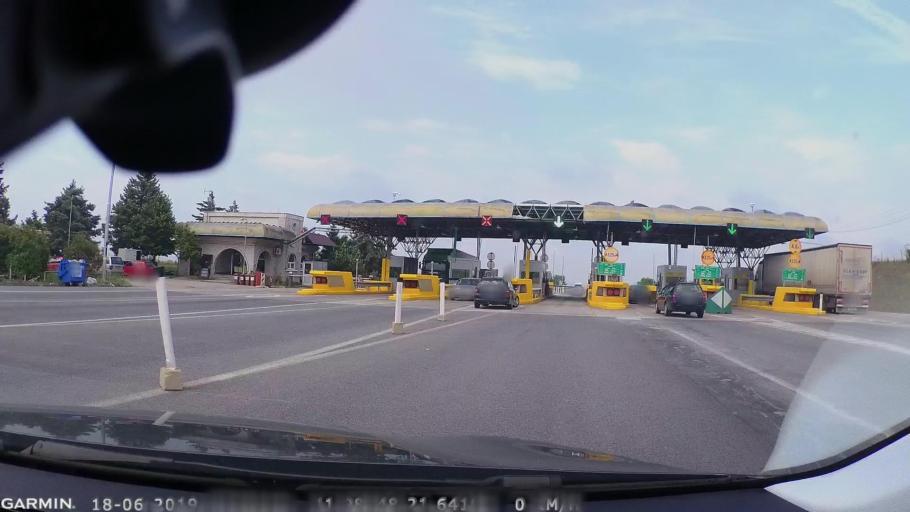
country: MK
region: Petrovec
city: Sredno Konjare
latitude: 41.9557
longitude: 21.7389
